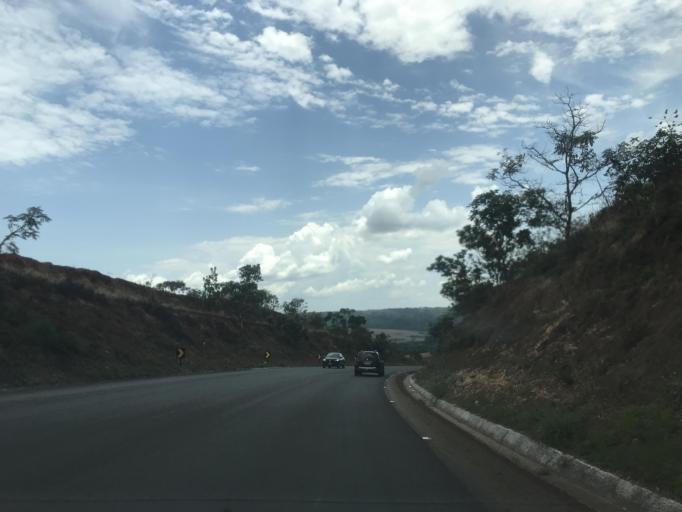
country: BR
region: Goias
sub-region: Vianopolis
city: Vianopolis
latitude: -16.9430
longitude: -48.5575
